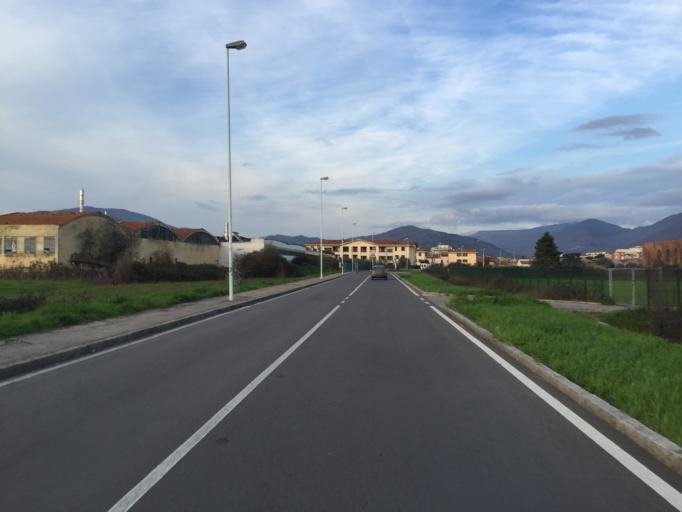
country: IT
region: Tuscany
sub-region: Provincia di Prato
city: Prato
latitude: 43.8799
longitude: 11.0788
